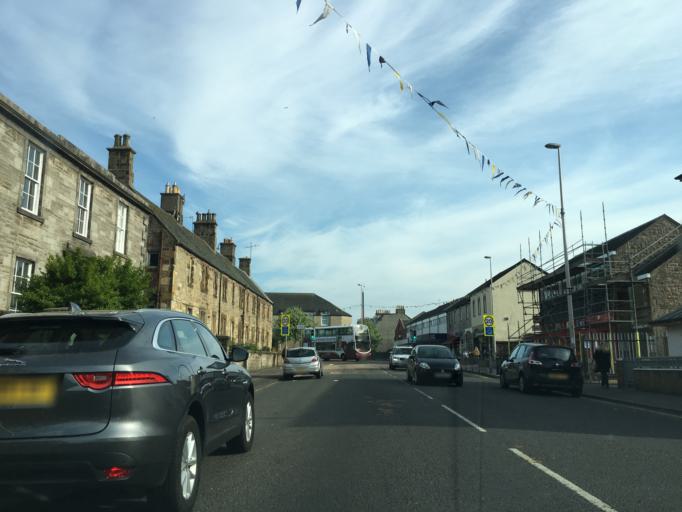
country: GB
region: Scotland
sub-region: Midlothian
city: Penicuik
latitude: 55.8285
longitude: -3.2229
